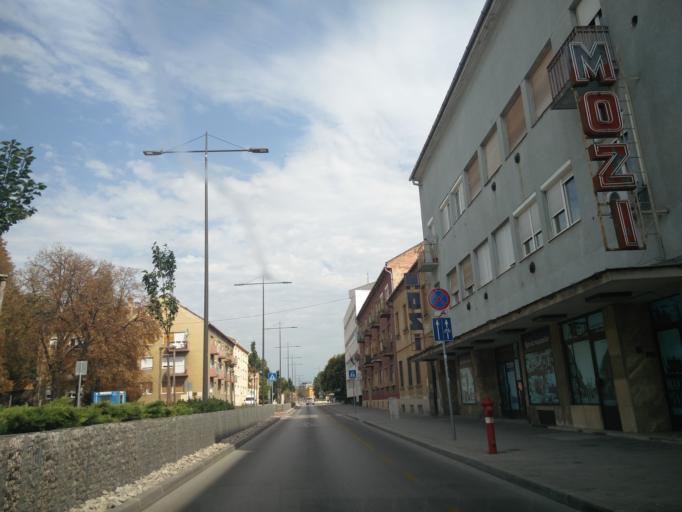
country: HU
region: Fejer
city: Szekesfehervar
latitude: 47.1906
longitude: 18.4127
